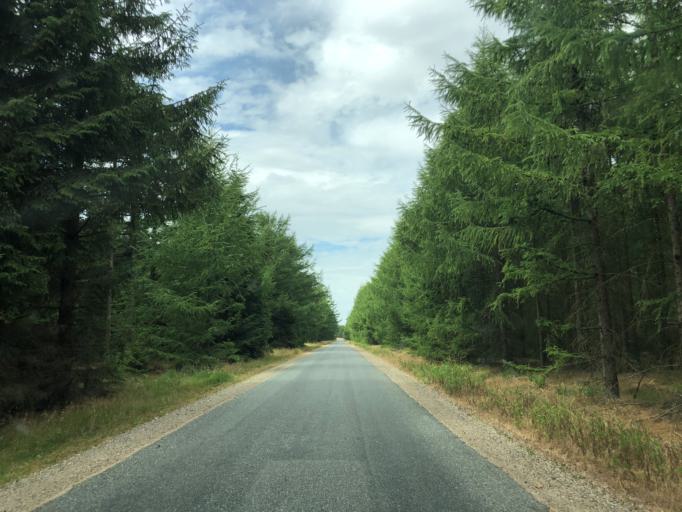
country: DK
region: South Denmark
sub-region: Billund Kommune
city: Grindsted
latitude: 55.6478
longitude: 8.8958
